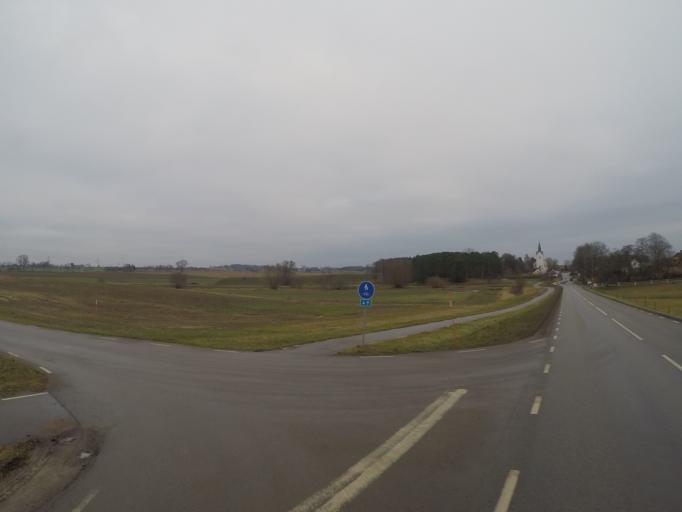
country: SE
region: Skane
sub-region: Hoors Kommun
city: Loberod
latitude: 55.7480
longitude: 13.3932
